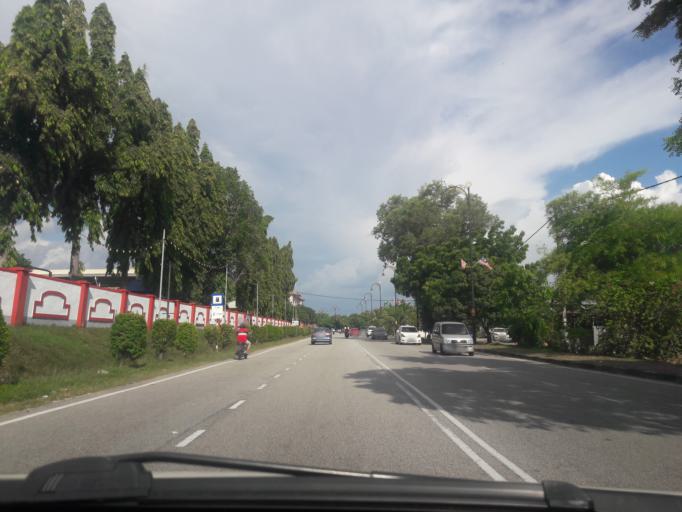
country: MY
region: Kedah
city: Sungai Petani
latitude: 5.6522
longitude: 100.5025
